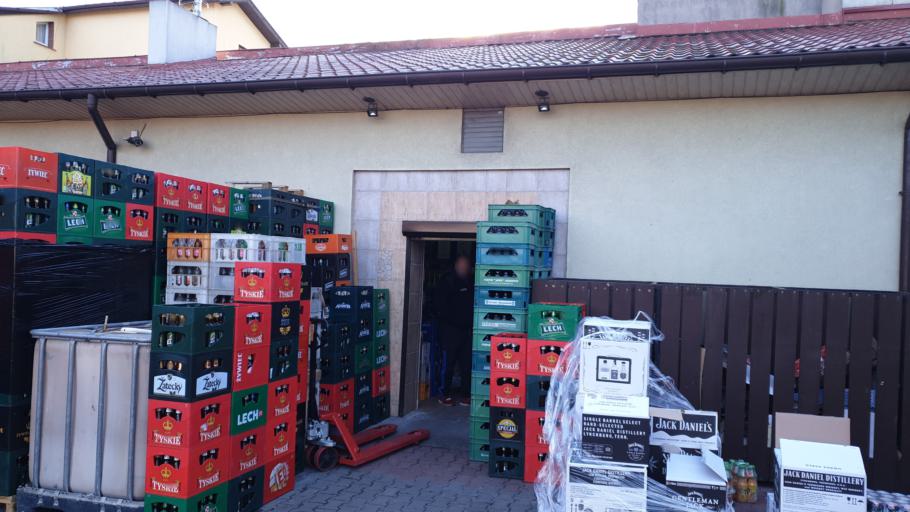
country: PL
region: Kujawsko-Pomorskie
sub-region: Powiat zninski
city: Znin
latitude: 52.8478
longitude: 17.7248
